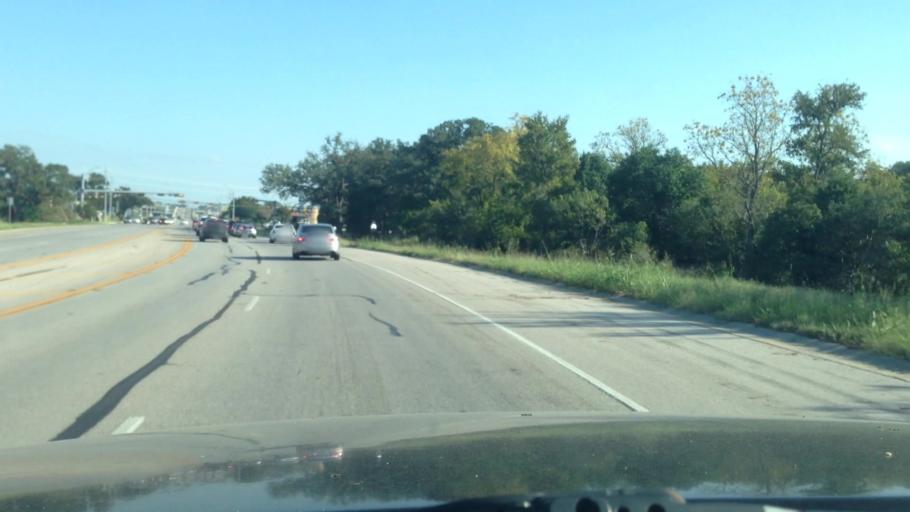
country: US
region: Texas
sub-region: Hays County
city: San Marcos
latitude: 29.8671
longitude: -97.9650
